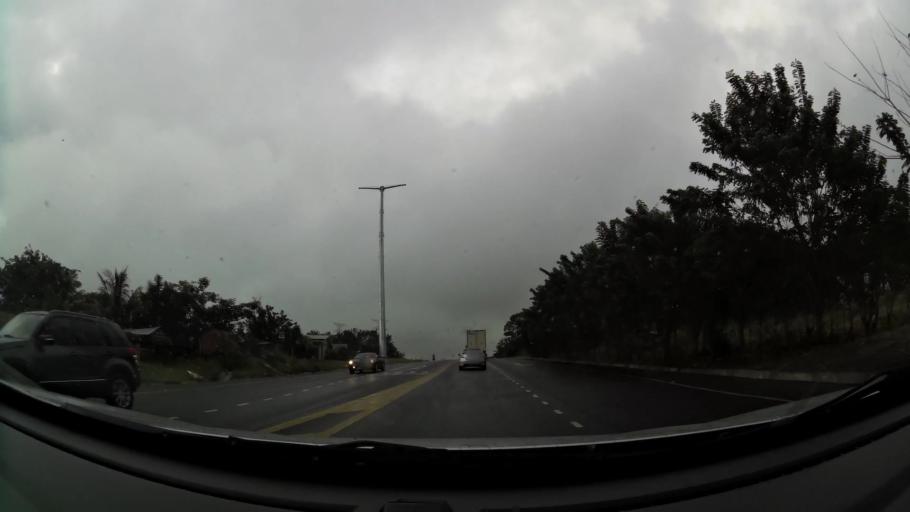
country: CR
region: Alajuela
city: Carrillos
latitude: 9.9892
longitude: -84.2692
